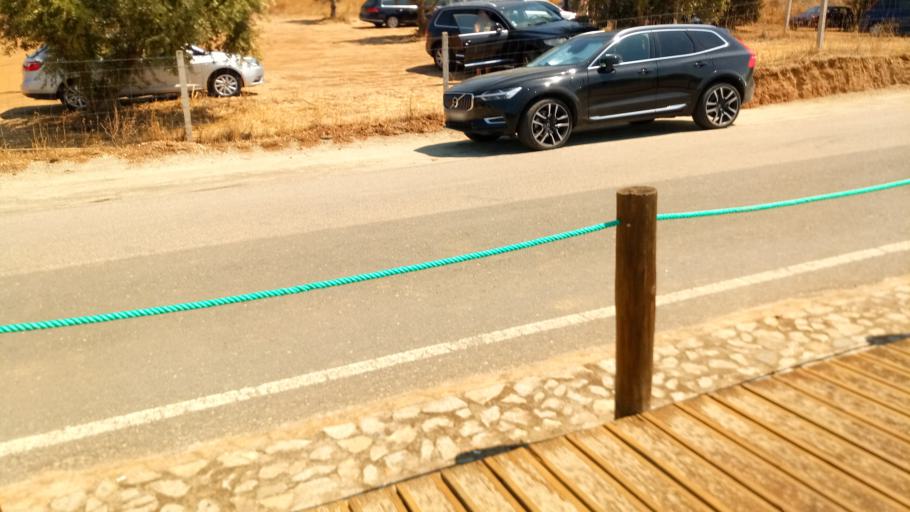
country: PT
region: Evora
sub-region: Reguengos de Monsaraz
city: Reguengos de Monsaraz
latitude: 38.2904
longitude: -7.5587
